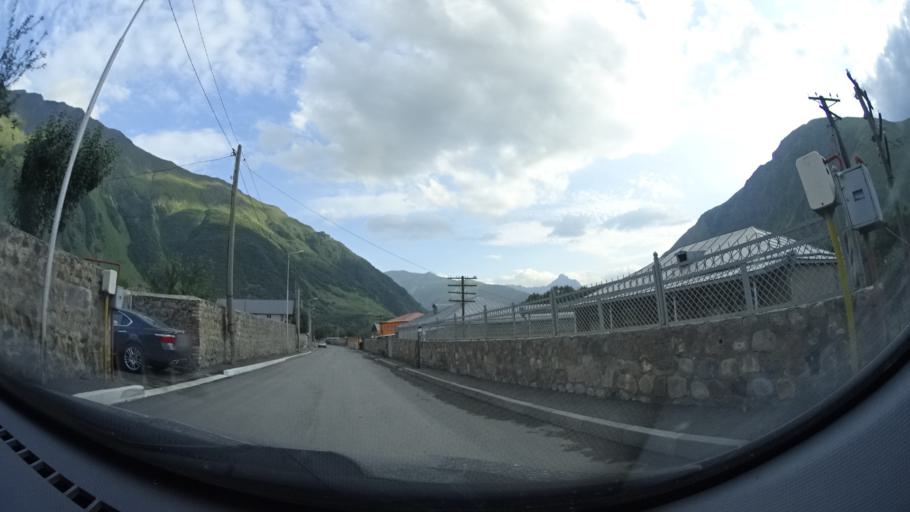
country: GE
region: Mtskheta-Mtianeti
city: Step'antsminda
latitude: 42.6541
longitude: 44.6417
